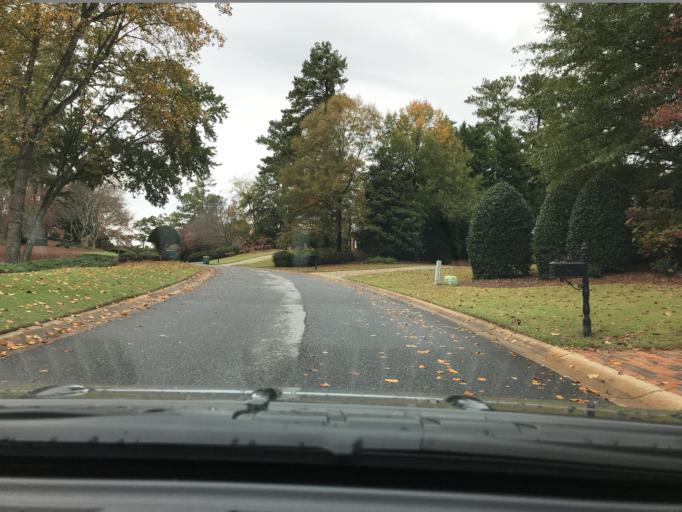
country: US
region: Georgia
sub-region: Fulton County
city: Johns Creek
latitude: 34.0129
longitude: -84.2485
